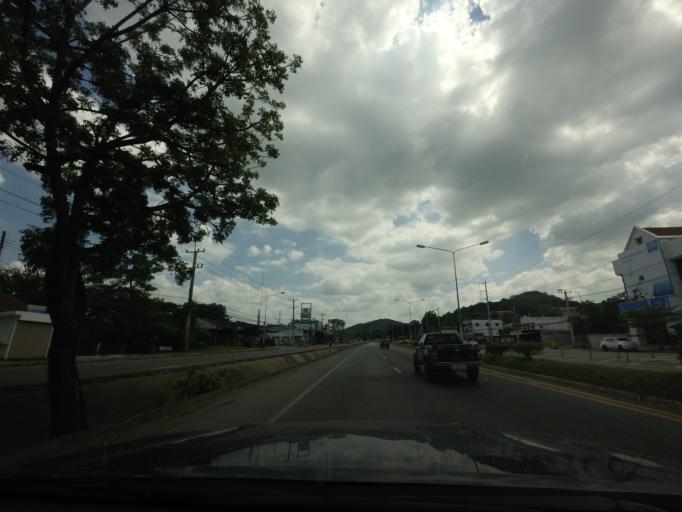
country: TH
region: Phetchabun
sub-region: Amphoe Bueng Sam Phan
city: Bueng Sam Phan
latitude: 15.7768
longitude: 101.0061
